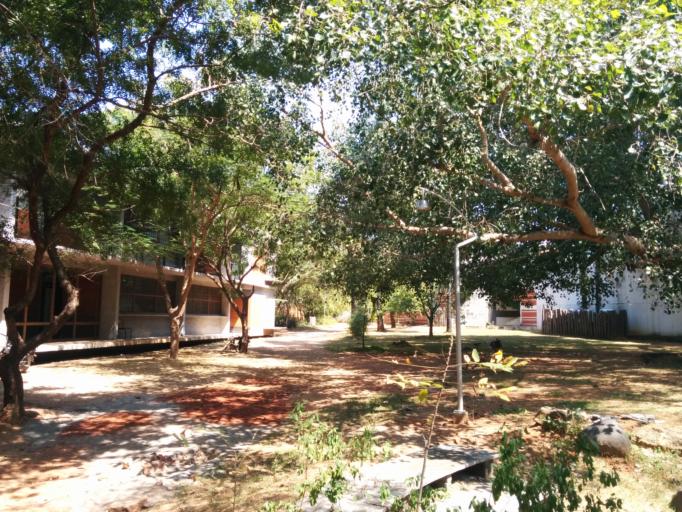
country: IN
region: Tamil Nadu
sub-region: Villupuram
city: Auroville
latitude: 12.0072
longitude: 79.8011
